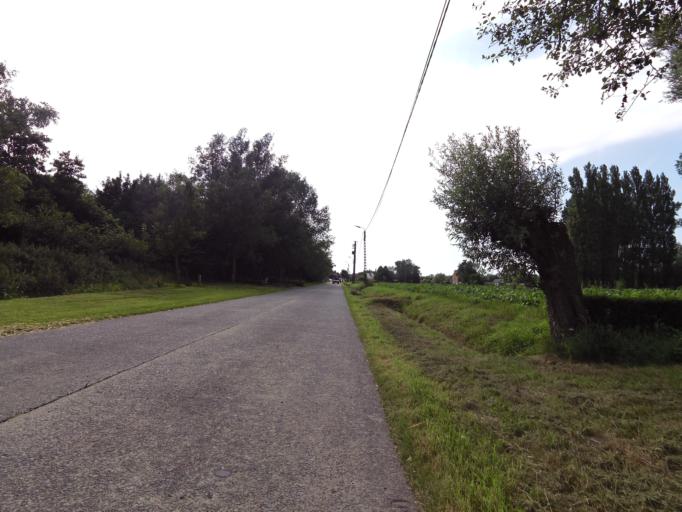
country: BE
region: Flanders
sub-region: Provincie West-Vlaanderen
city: Oudenburg
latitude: 51.1788
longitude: 3.0433
